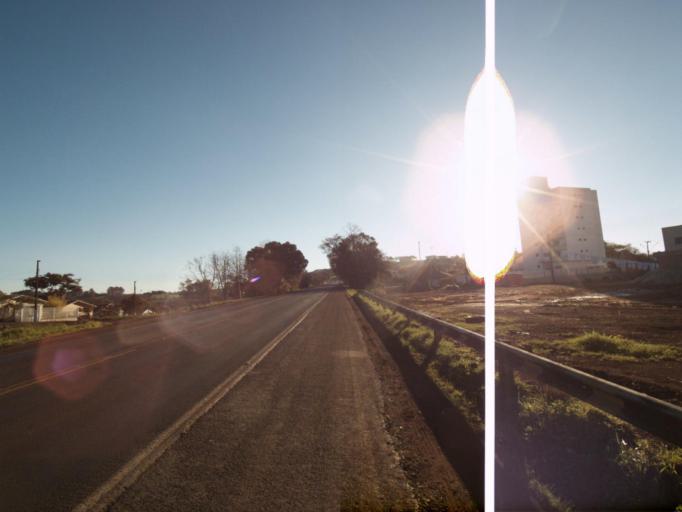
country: BR
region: Santa Catarina
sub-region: Chapeco
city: Chapeco
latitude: -26.9047
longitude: -52.9060
